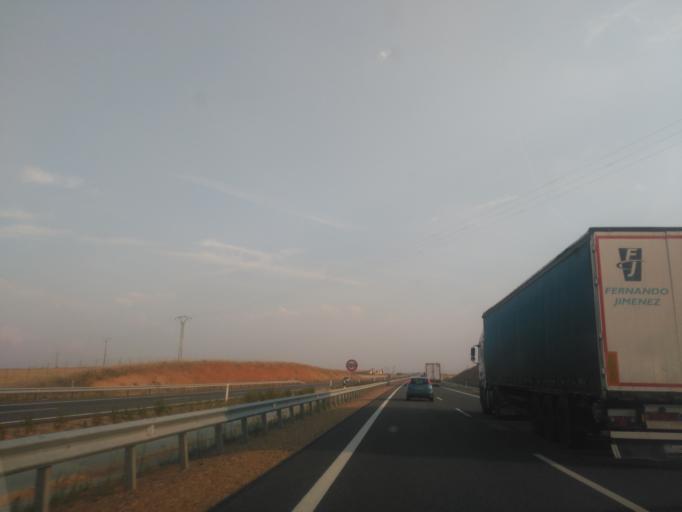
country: ES
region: Castille and Leon
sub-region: Provincia de Zamora
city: Montamarta
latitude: 41.6526
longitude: -5.7946
